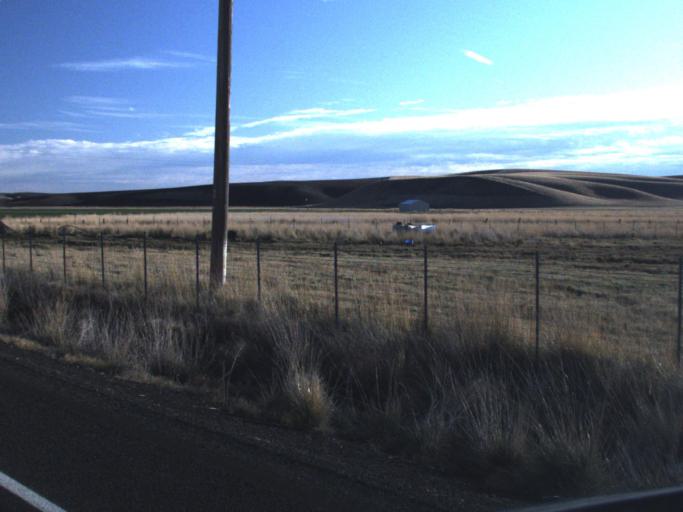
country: US
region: Washington
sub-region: Whitman County
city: Colfax
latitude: 46.8030
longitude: -117.6642
